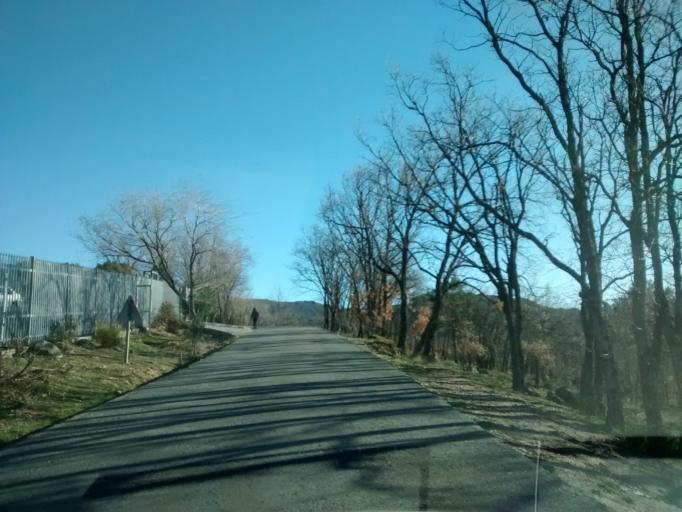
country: ES
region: Madrid
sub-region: Provincia de Madrid
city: Navacerrada
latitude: 40.7394
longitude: -4.0052
